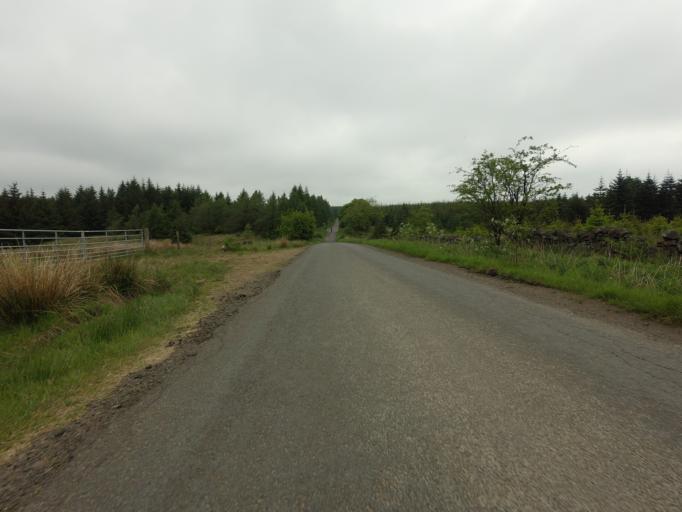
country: GB
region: Scotland
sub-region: Fife
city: Townhill
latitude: 56.1359
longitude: -3.4442
